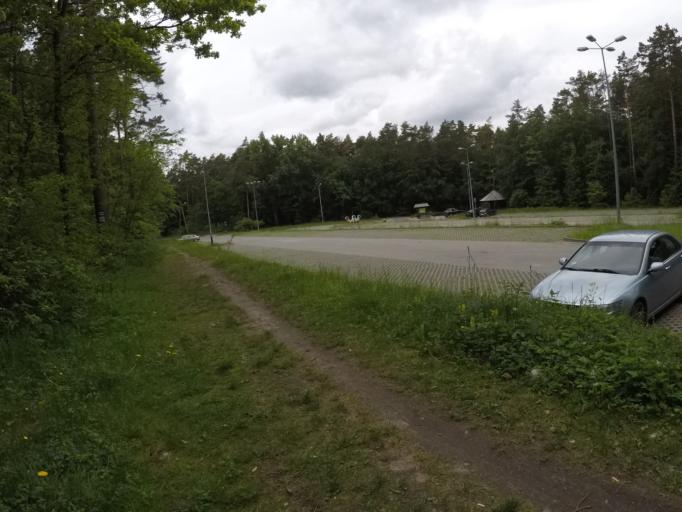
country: PL
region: Swietokrzyskie
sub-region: Powiat kielecki
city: Kielce
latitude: 50.8410
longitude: 20.6083
